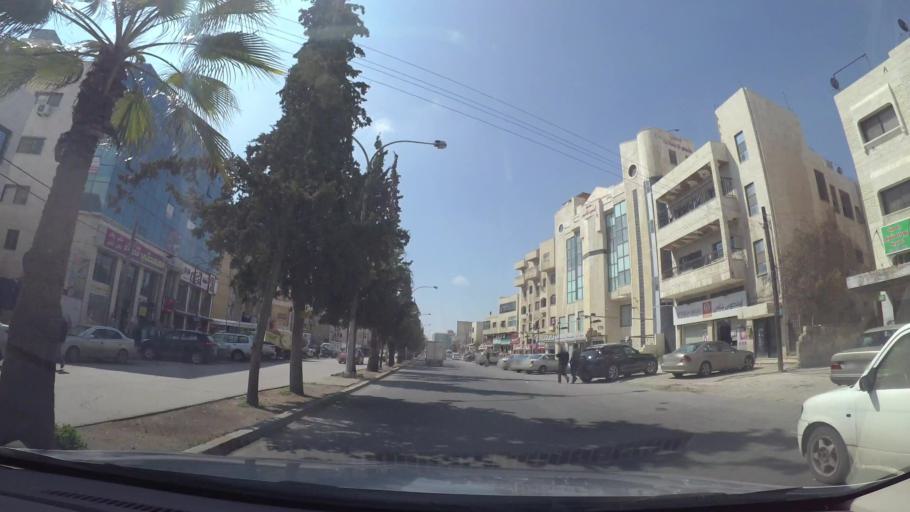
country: JO
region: Amman
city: Al Bunayyat ash Shamaliyah
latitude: 31.9280
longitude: 35.9075
